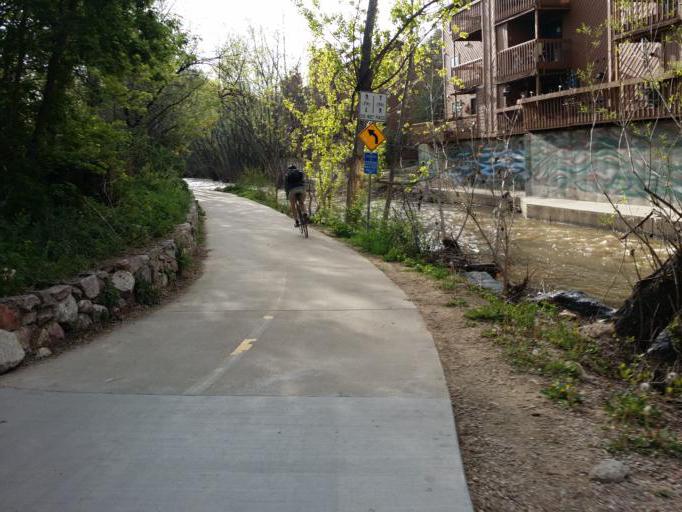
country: US
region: Colorado
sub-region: Boulder County
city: Boulder
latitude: 40.0110
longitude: -105.2568
